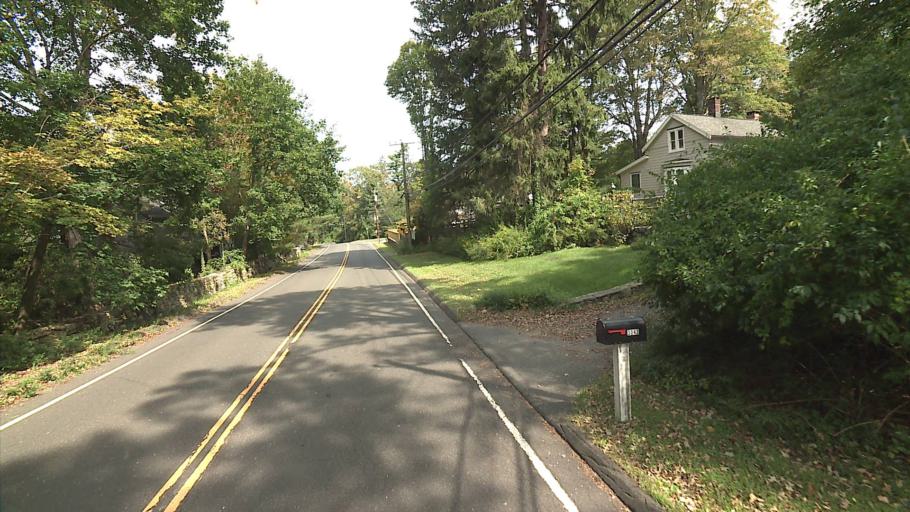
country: US
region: Connecticut
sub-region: Fairfield County
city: North Stamford
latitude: 41.1699
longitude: -73.5634
